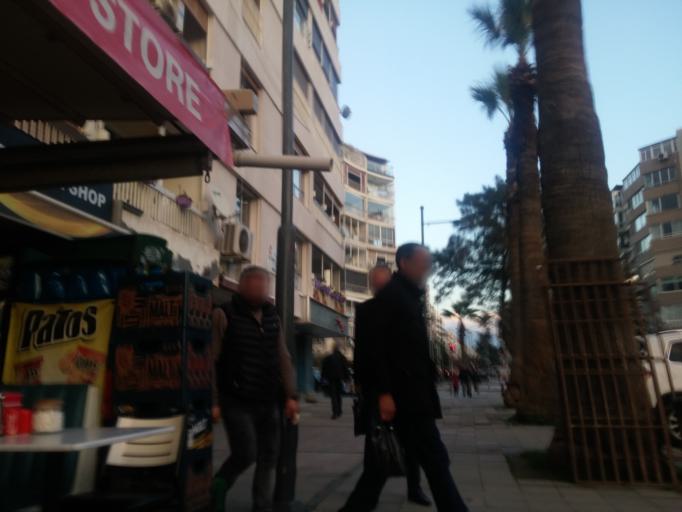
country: TR
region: Izmir
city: Izmir
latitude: 38.4332
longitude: 27.1381
